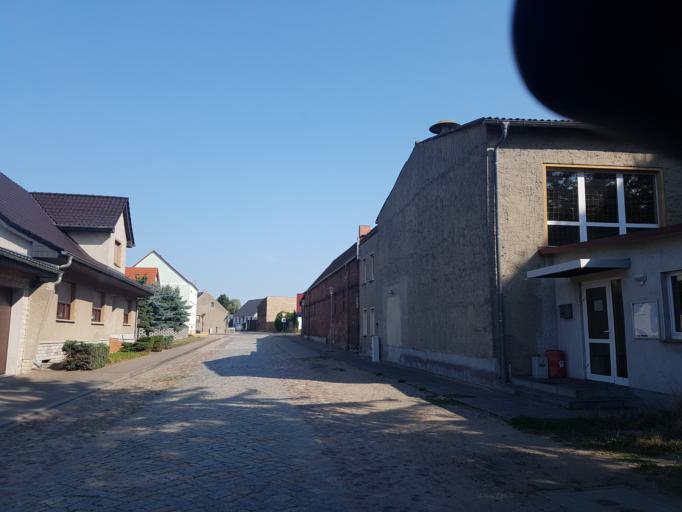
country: DE
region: Brandenburg
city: Niemegk
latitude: 52.1002
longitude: 12.6648
